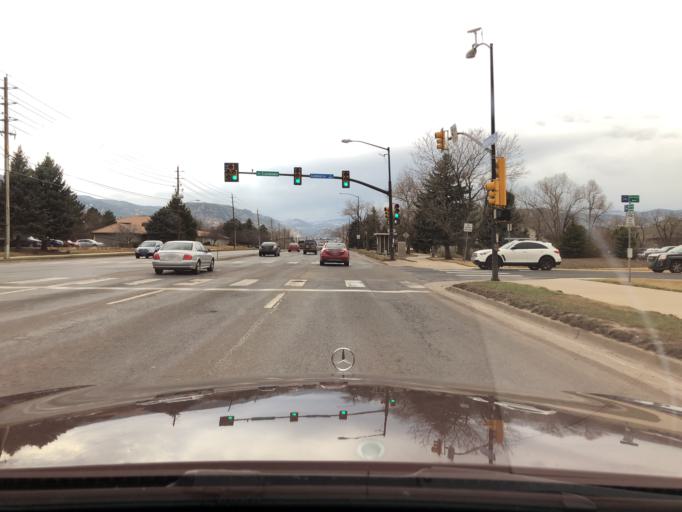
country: US
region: Colorado
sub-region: Boulder County
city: Boulder
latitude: 40.0148
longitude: -105.2314
